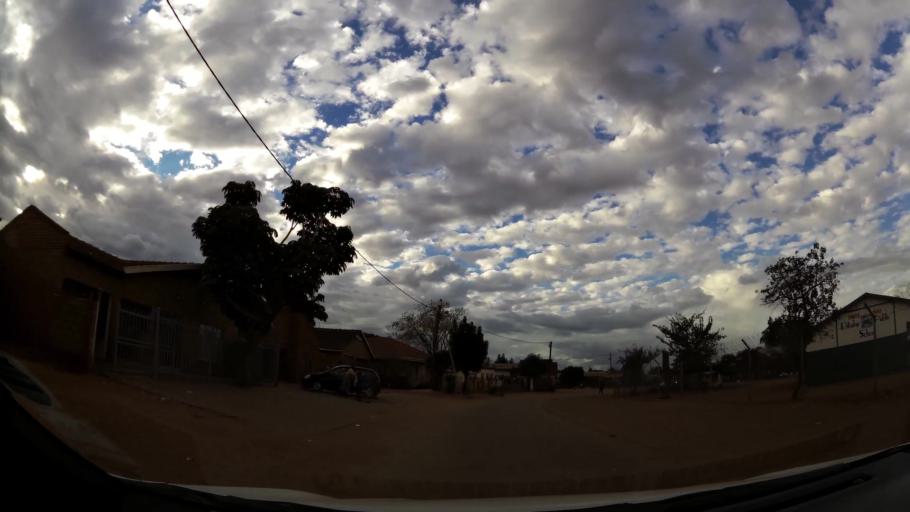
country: ZA
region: Limpopo
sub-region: Waterberg District Municipality
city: Modimolle
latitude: -24.5229
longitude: 28.7229
